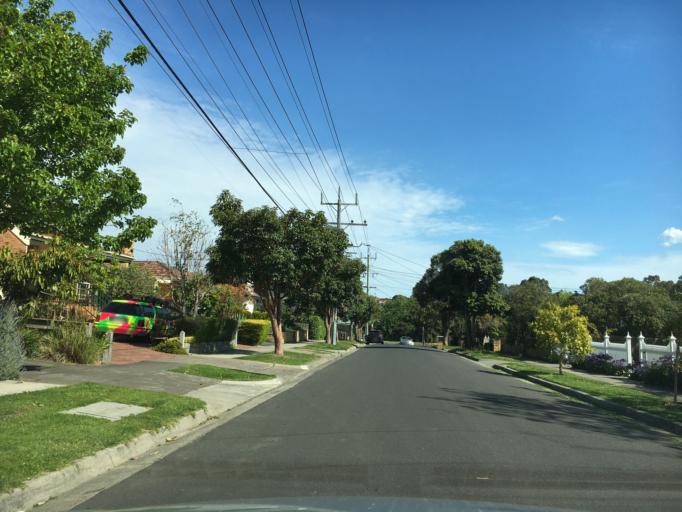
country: AU
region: Victoria
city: Clayton
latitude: -37.8967
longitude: 145.1141
